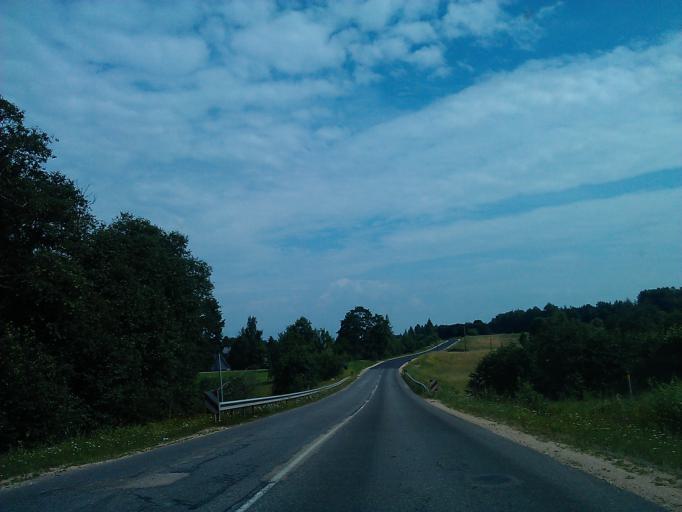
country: LV
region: Priekuli
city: Priekuli
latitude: 57.3353
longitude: 25.3270
